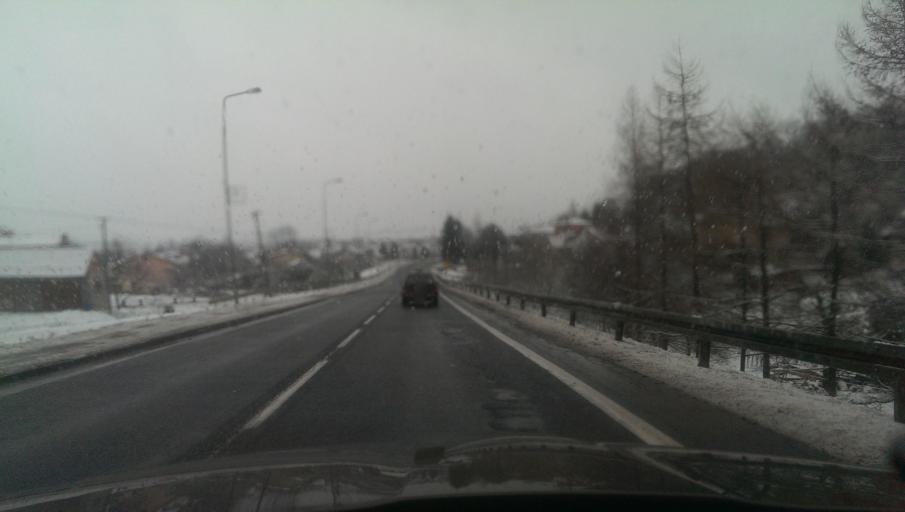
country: PL
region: Subcarpathian Voivodeship
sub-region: Powiat sanocki
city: Besko
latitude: 49.5861
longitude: 21.9440
